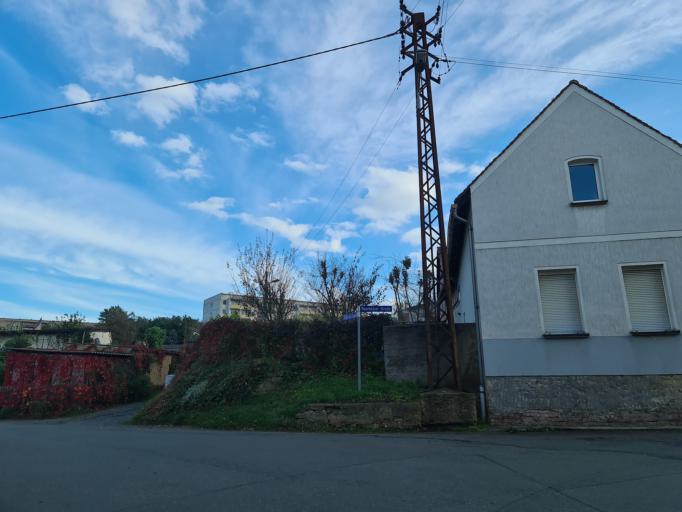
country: DE
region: Thuringia
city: Gera
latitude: 50.9075
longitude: 12.0846
